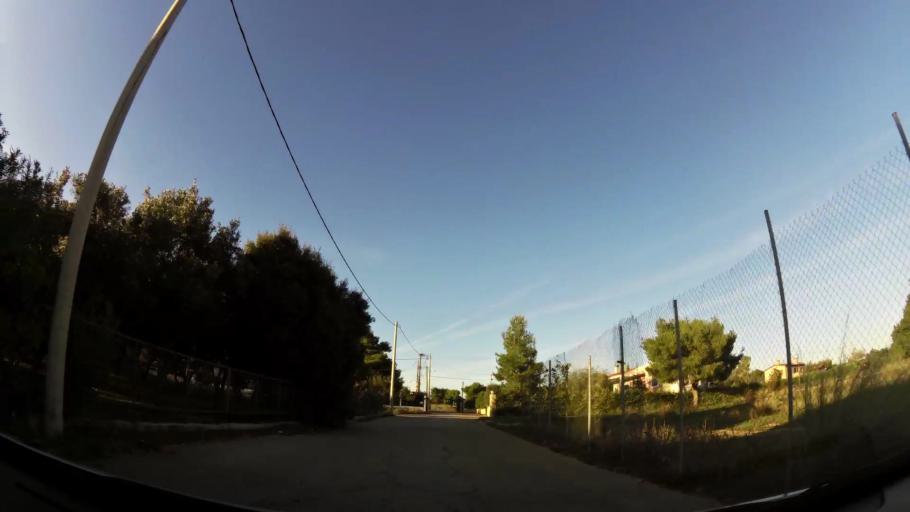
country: GR
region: Attica
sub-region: Nomarchia Anatolikis Attikis
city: Kryoneri
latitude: 38.1285
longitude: 23.8253
